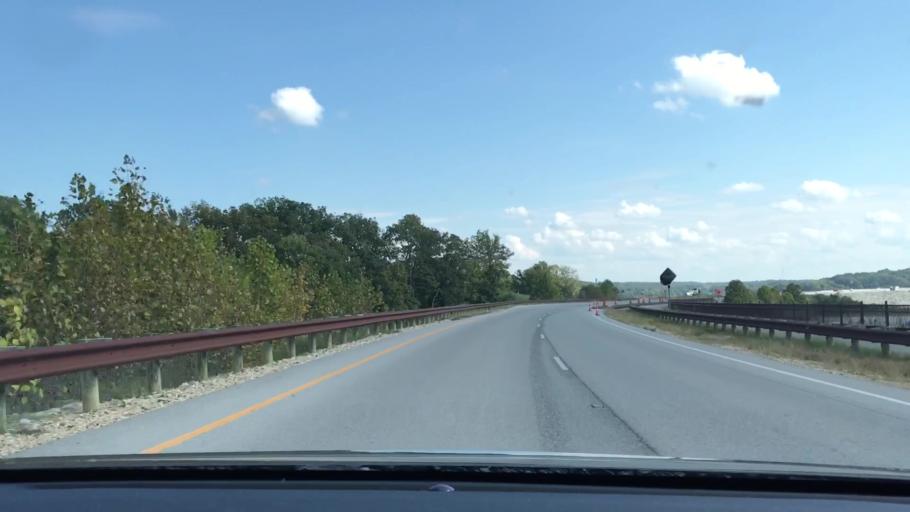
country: US
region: Kentucky
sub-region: Trigg County
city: Cadiz
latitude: 36.8012
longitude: -87.9891
